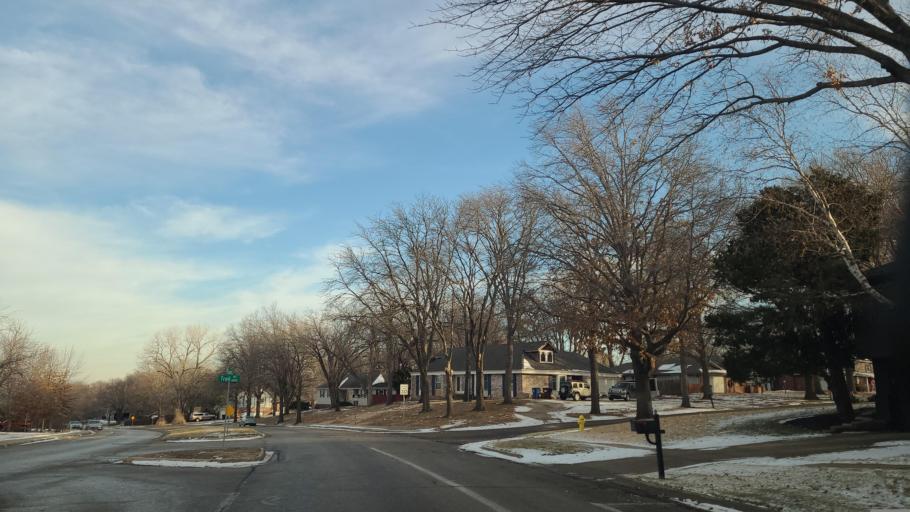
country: US
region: Kansas
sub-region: Douglas County
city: Lawrence
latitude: 38.9750
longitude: -95.2718
